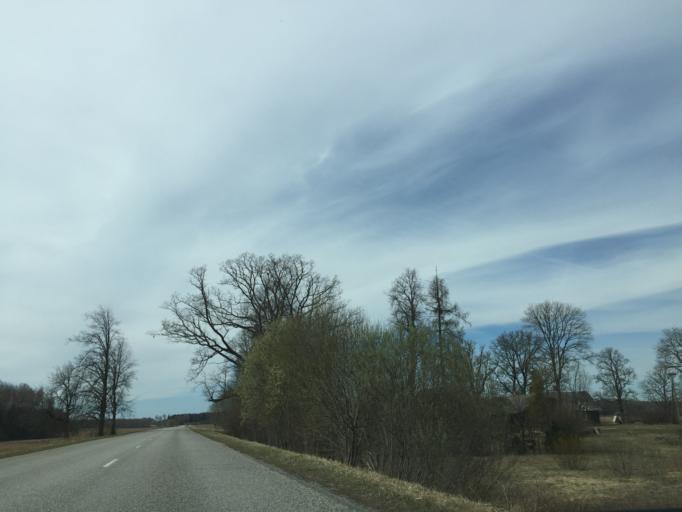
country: LV
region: Valkas Rajons
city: Valka
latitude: 57.7801
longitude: 25.9682
